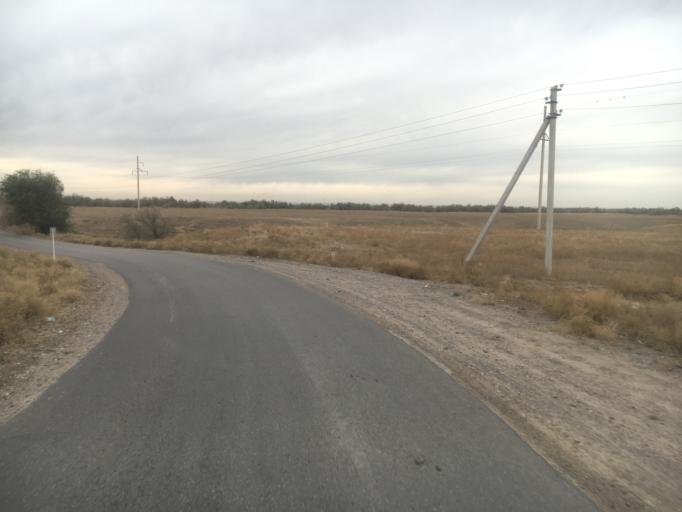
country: KZ
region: Almaty Oblysy
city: Energeticheskiy
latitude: 43.5854
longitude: 77.0867
